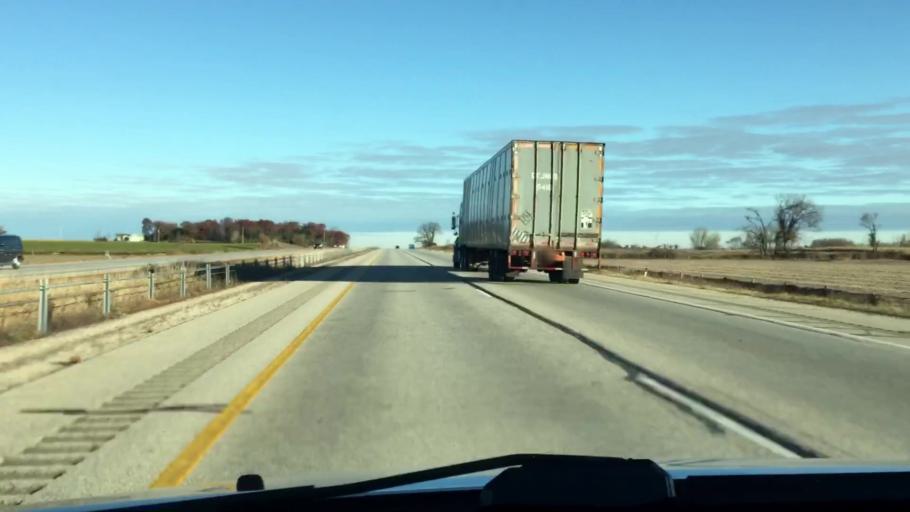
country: US
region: Wisconsin
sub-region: Dodge County
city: Lomira
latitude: 43.6694
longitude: -88.4417
